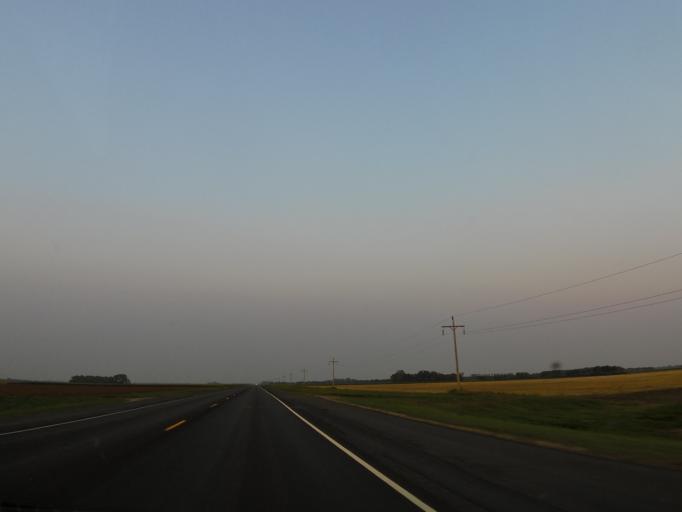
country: US
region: North Dakota
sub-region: Walsh County
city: Park River
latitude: 48.4126
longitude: -97.5964
